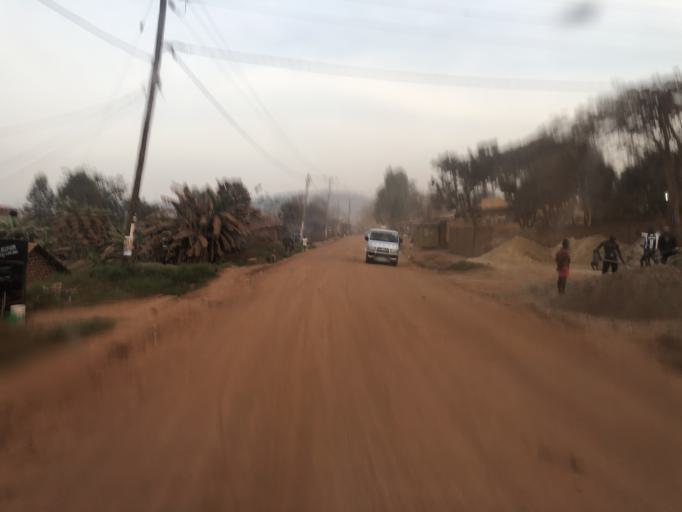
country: UG
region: Central Region
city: Kampala Central Division
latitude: 0.2989
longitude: 32.5180
